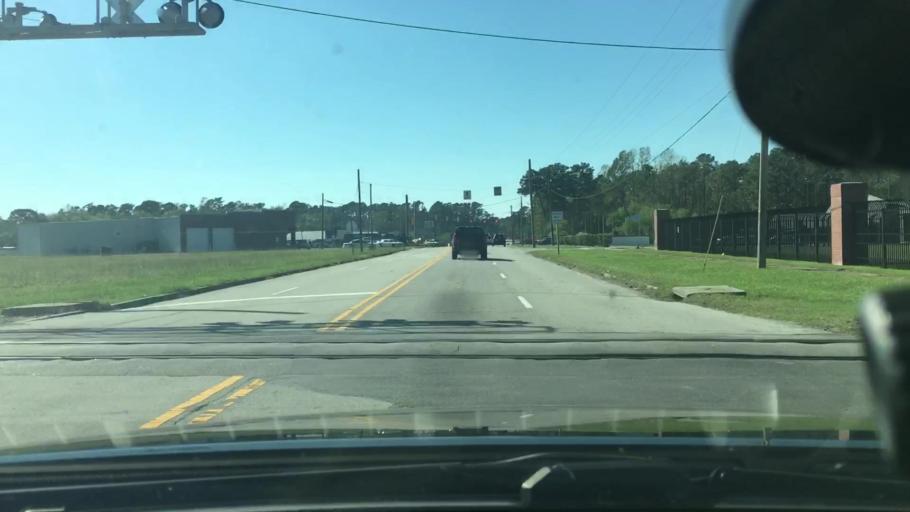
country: US
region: North Carolina
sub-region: Craven County
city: Havelock
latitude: 34.8826
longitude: -76.9041
